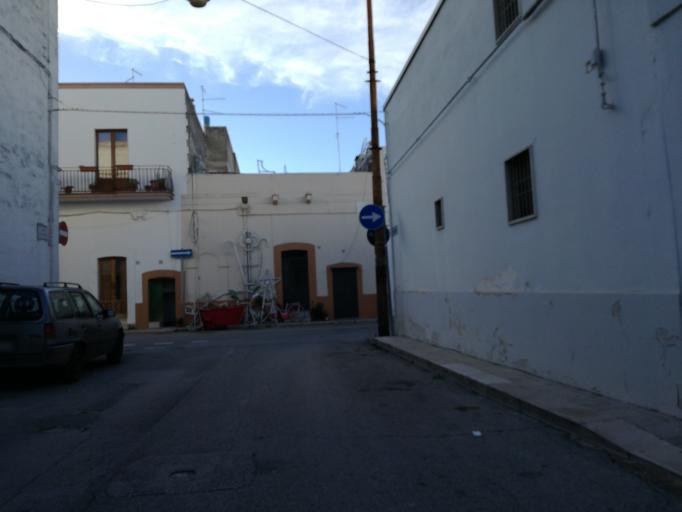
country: IT
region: Apulia
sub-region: Provincia di Bari
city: Adelfia
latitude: 41.0008
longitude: 16.8678
